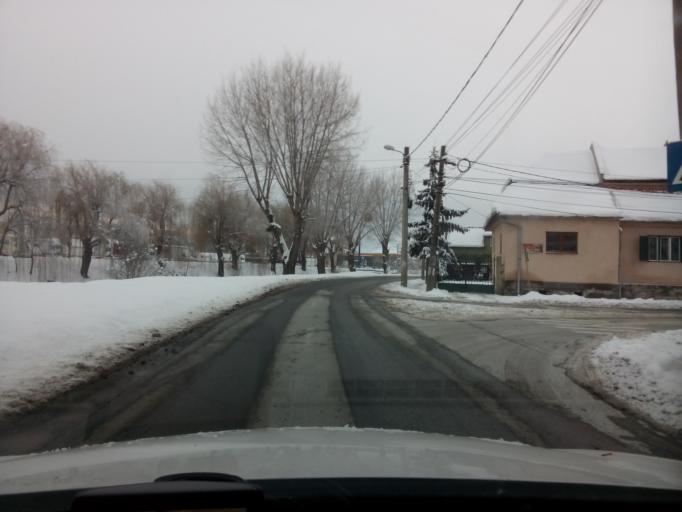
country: RO
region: Sibiu
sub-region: Municipiul Sibiu
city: Sibiu
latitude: 45.7976
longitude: 24.1417
